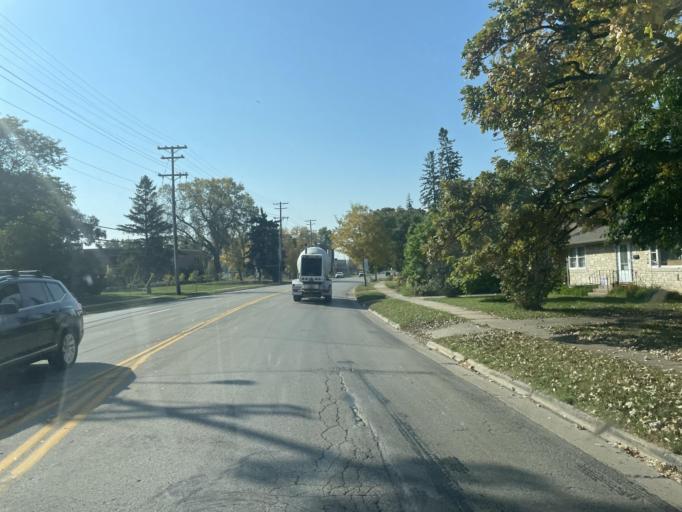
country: US
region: Wisconsin
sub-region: Dane County
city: Madison
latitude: 43.0515
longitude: -89.3992
